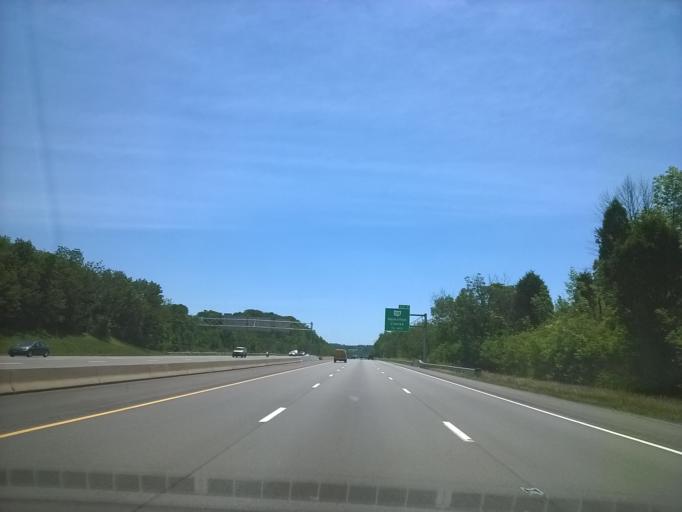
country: US
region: Ohio
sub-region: Hamilton County
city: Grandview
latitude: 39.2131
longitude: -84.7245
